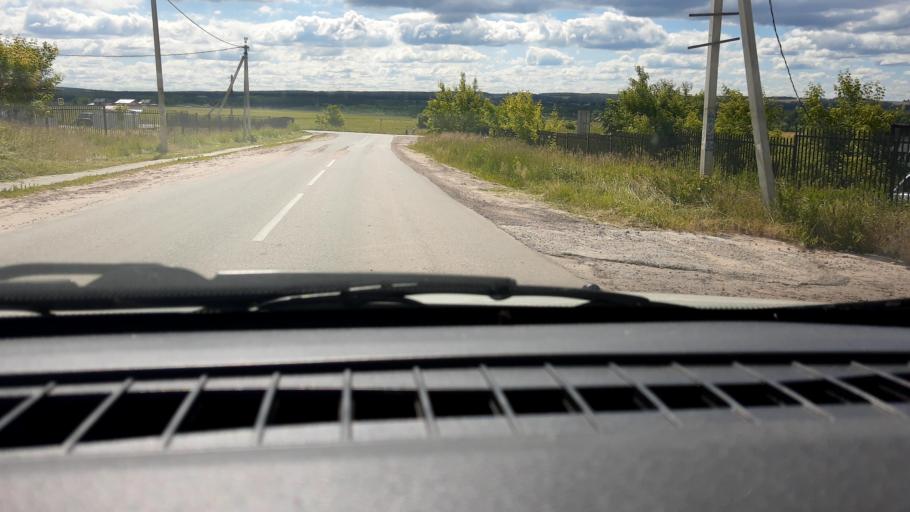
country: RU
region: Nizjnij Novgorod
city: Burevestnik
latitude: 56.0598
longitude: 43.8659
